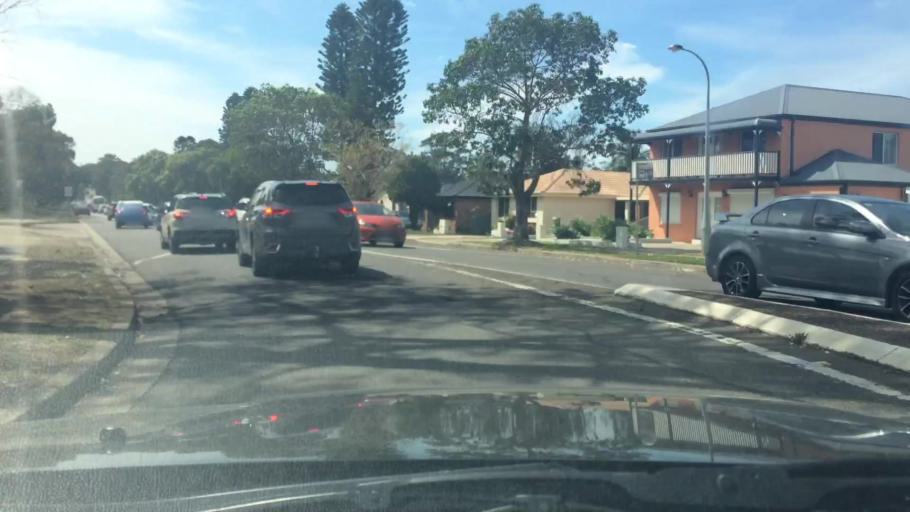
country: AU
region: New South Wales
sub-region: Fairfield
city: Cabramatta West
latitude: -33.8637
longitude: 150.8986
